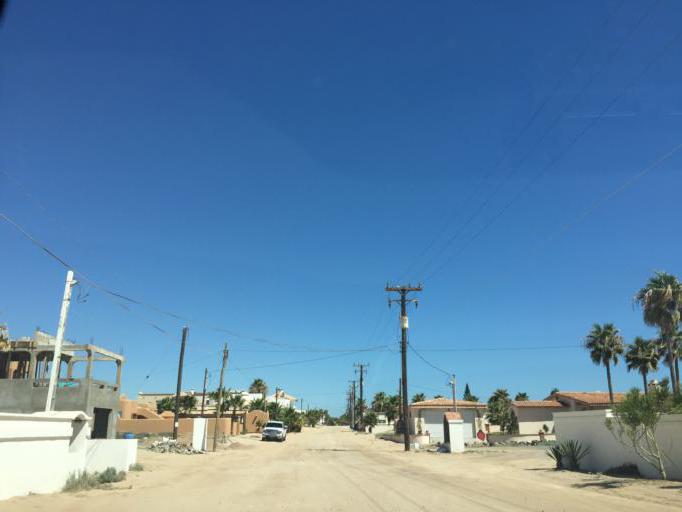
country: MX
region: Sonora
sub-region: Puerto Penasco
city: Puerto Penasco
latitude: 31.2938
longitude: -113.5177
